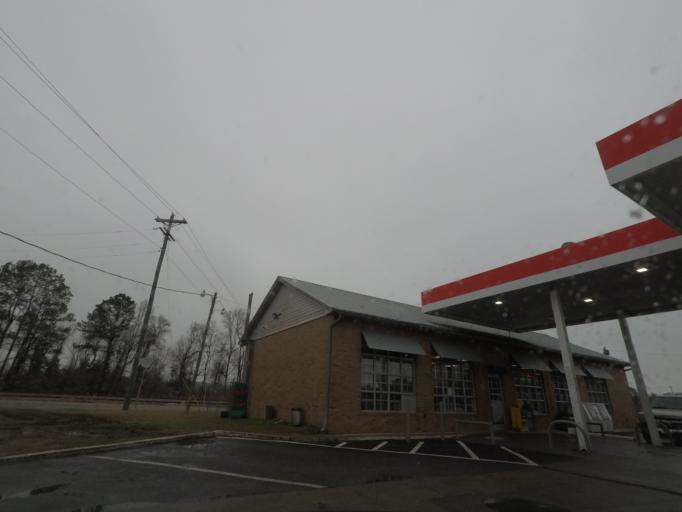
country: US
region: South Carolina
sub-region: Clarendon County
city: Manning
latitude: 33.7422
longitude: -80.2108
